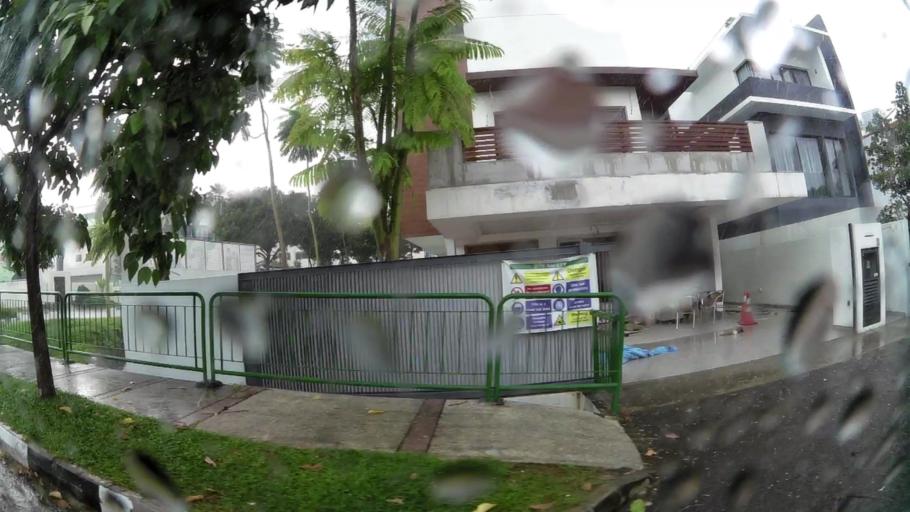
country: SG
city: Singapore
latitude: 1.3308
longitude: 103.9426
